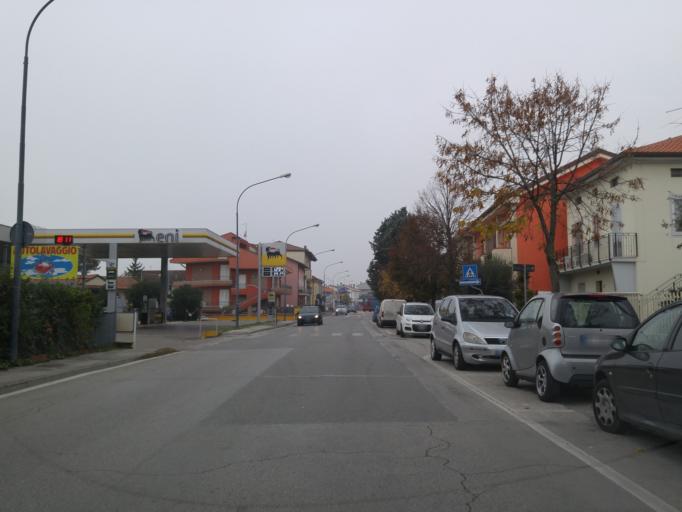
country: IT
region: The Marches
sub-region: Provincia di Pesaro e Urbino
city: Gabicce Mare
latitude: 43.9599
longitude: 12.7525
